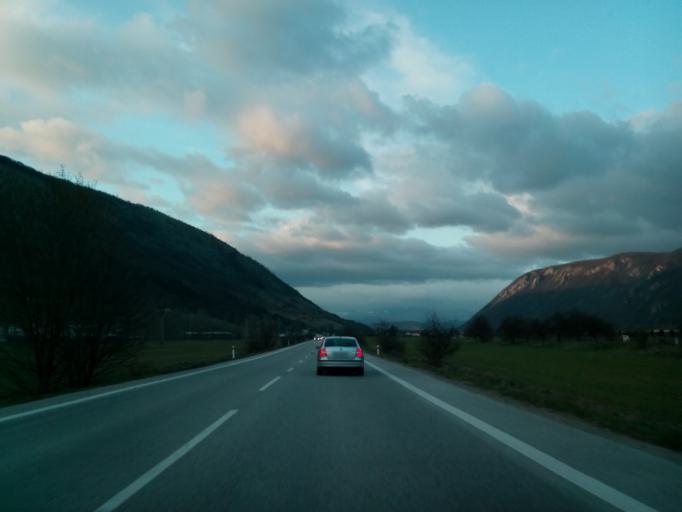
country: SK
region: Kosicky
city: Roznava
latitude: 48.5763
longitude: 20.4616
